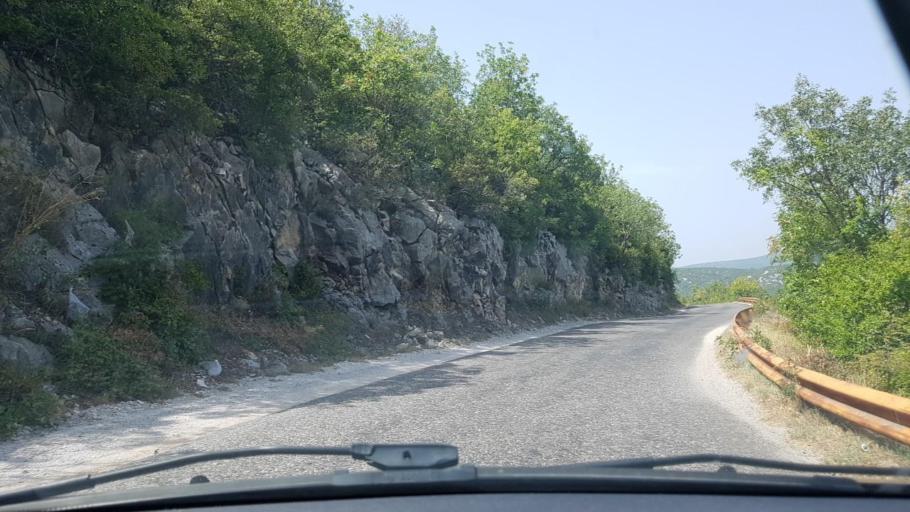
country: BA
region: Federation of Bosnia and Herzegovina
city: Tasovcici
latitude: 43.0137
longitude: 17.7859
